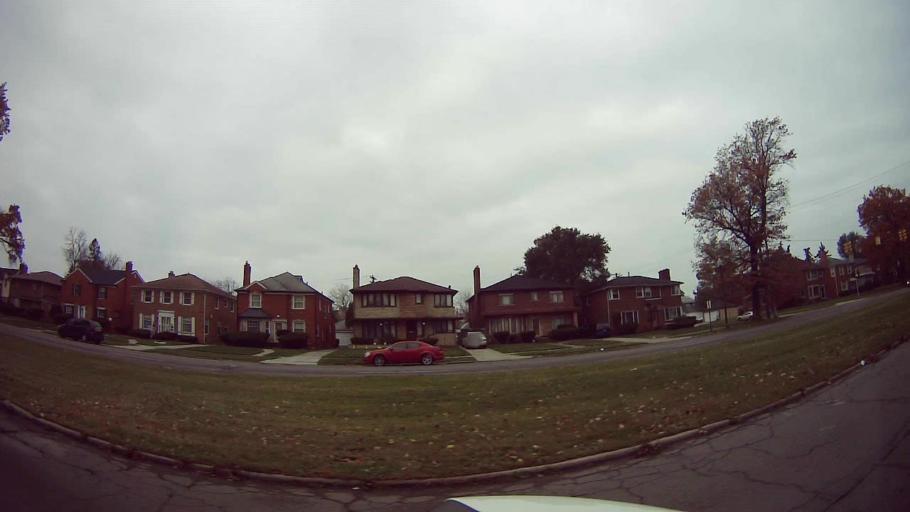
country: US
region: Michigan
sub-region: Oakland County
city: Oak Park
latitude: 42.4235
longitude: -83.1751
